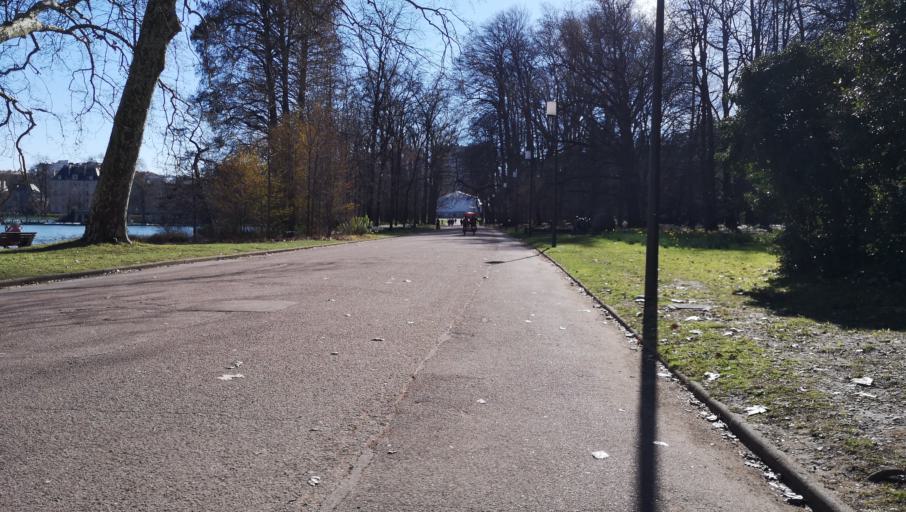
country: FR
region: Rhone-Alpes
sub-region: Departement du Rhone
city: Caluire-et-Cuire
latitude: 45.7798
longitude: 4.8482
